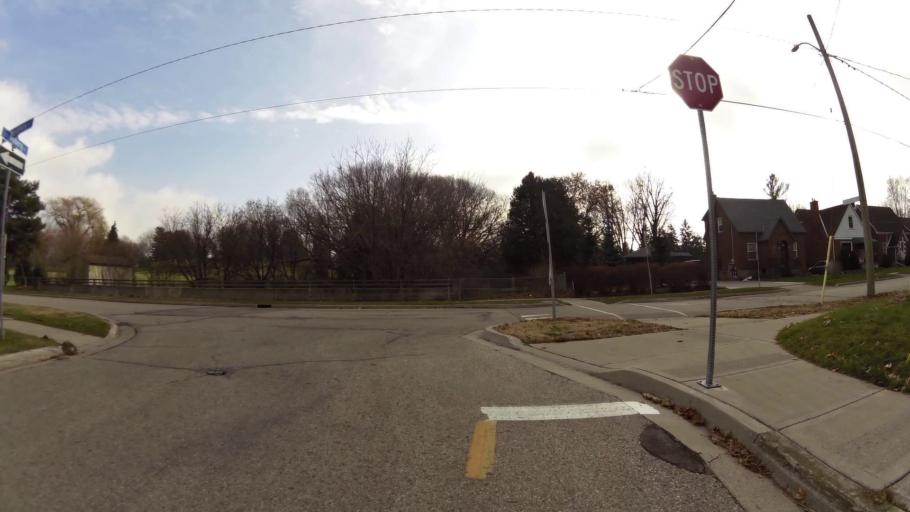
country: CA
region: Ontario
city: Kitchener
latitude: 43.4378
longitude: -80.4735
